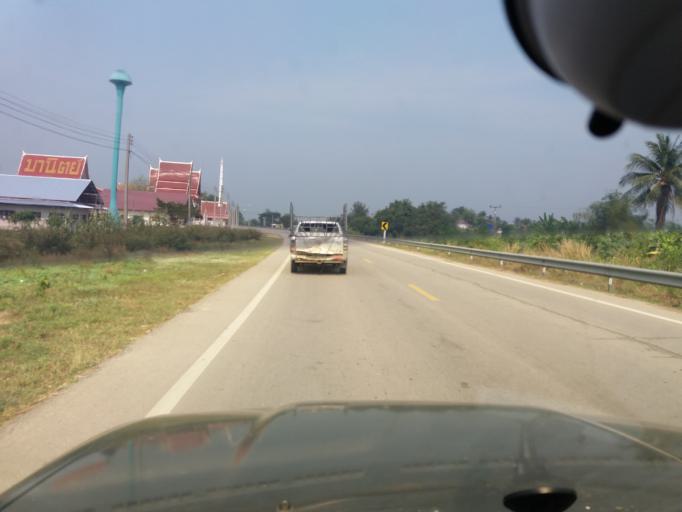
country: TH
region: Sing Buri
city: Bang Racham
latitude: 14.9010
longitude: 100.2684
